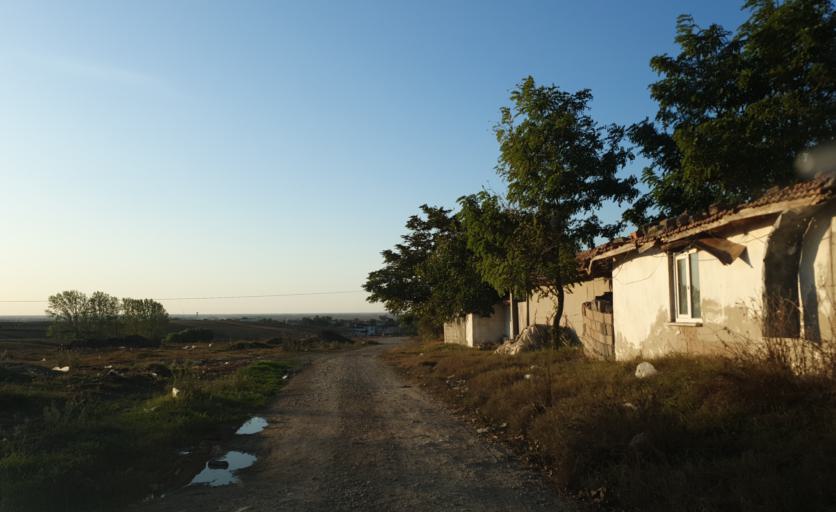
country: TR
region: Tekirdag
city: Beyazkoy
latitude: 41.3303
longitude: 27.7443
